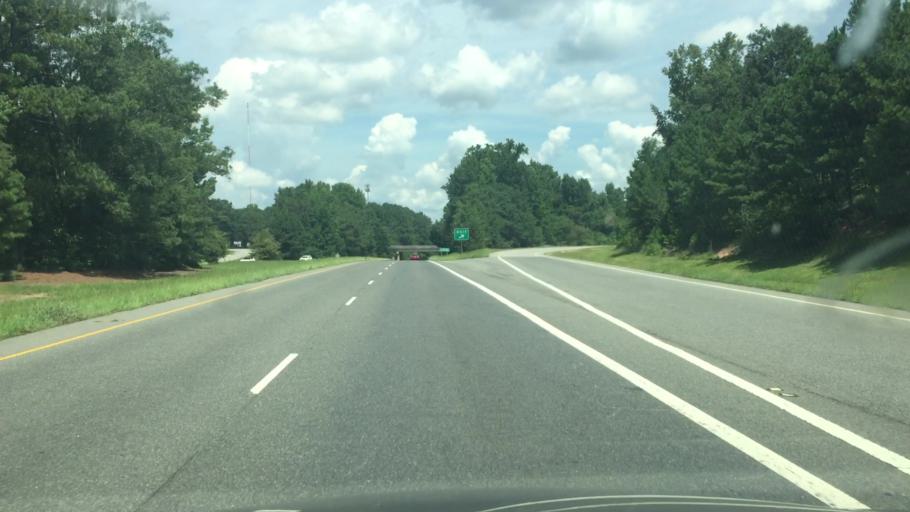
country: US
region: North Carolina
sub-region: Richmond County
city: Rockingham
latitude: 34.9285
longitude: -79.7800
